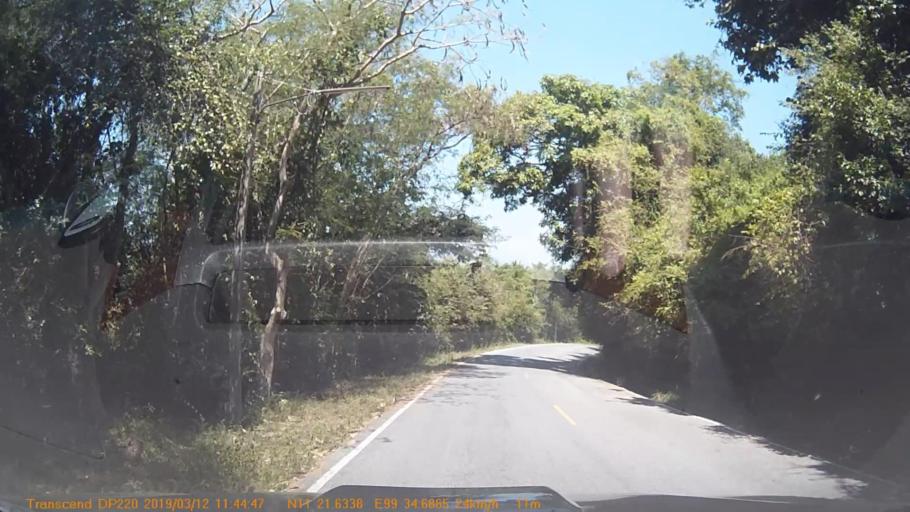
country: TH
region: Prachuap Khiri Khan
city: Thap Sakae
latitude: 11.3606
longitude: 99.5781
